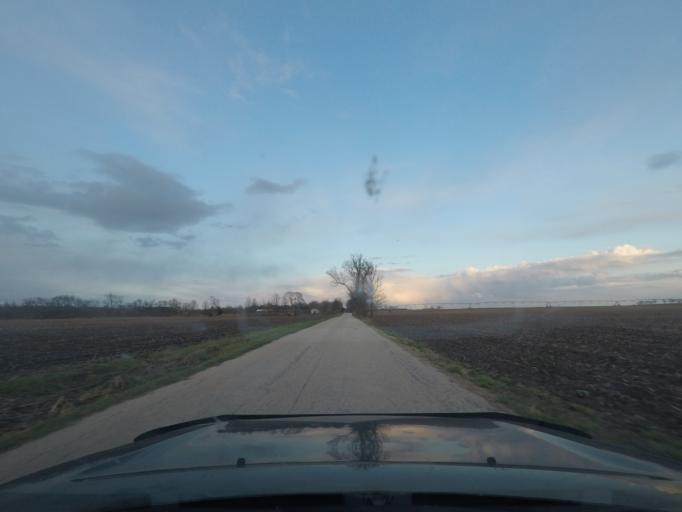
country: US
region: Indiana
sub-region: LaPorte County
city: Kingsford Heights
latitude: 41.4620
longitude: -86.7263
